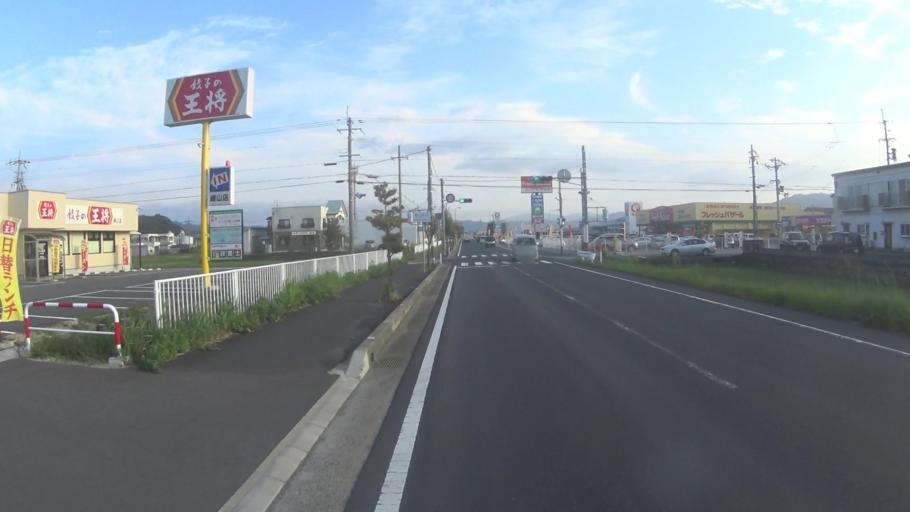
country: JP
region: Kyoto
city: Miyazu
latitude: 35.6181
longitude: 135.0760
